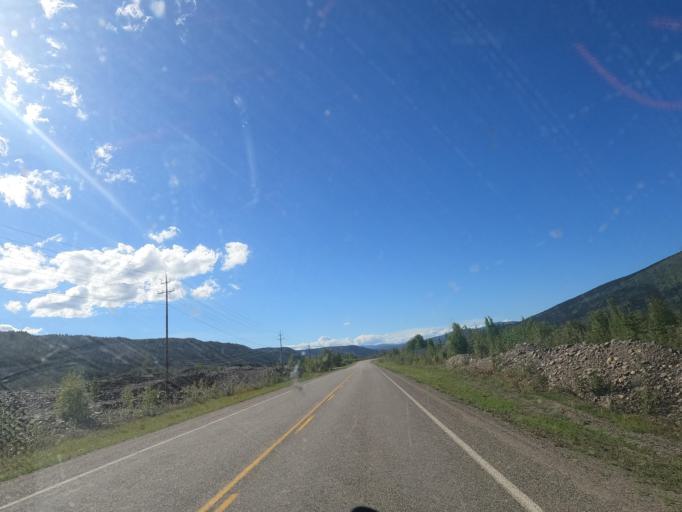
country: CA
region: Yukon
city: Dawson City
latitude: 64.0343
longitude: -139.2759
